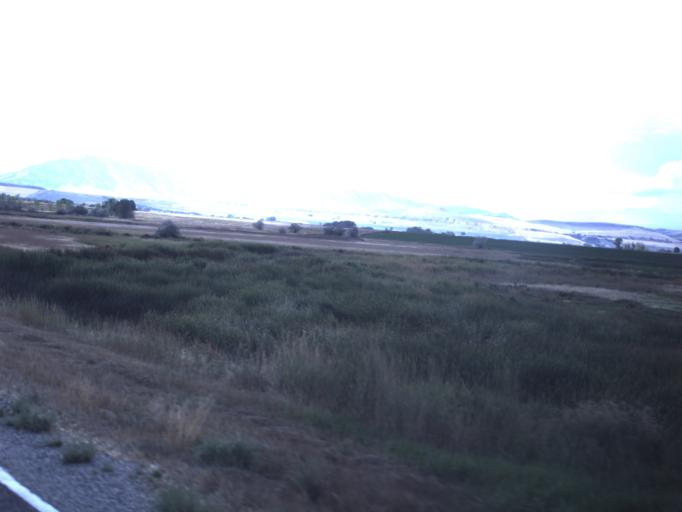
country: US
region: Utah
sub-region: Cache County
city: Lewiston
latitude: 41.9244
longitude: -111.9021
